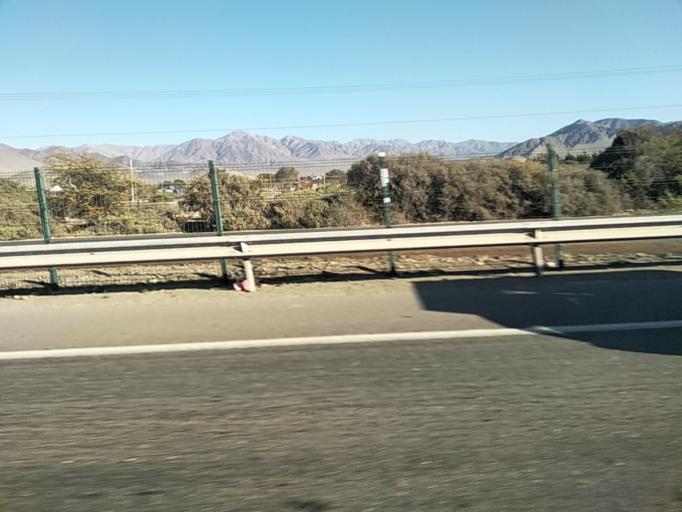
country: CL
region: Atacama
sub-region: Provincia de Copiapo
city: Copiapo
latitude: -27.3188
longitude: -70.5250
